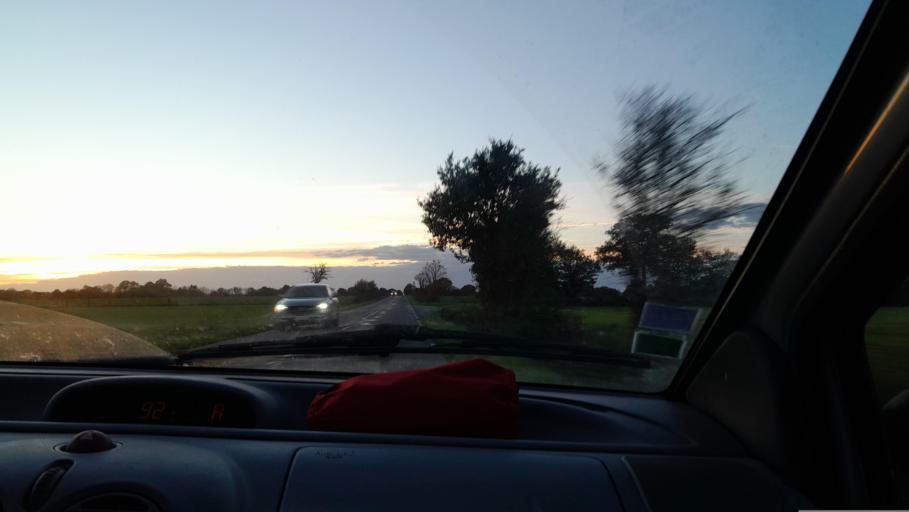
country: FR
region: Pays de la Loire
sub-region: Departement de la Mayenne
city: Ballots
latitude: 47.9018
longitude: -1.1270
